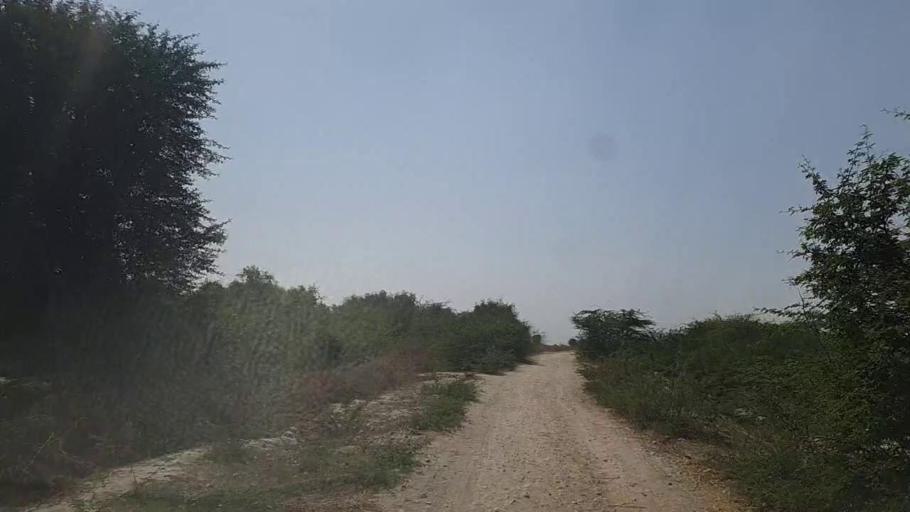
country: PK
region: Sindh
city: Naukot
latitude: 24.6519
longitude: 69.2843
